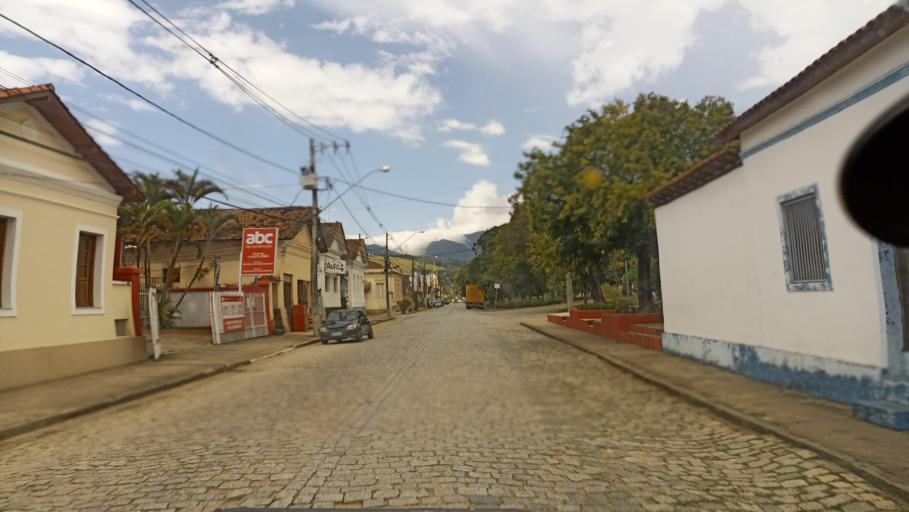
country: BR
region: Minas Gerais
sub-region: Passa Quatro
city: Passa Quatro
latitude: -22.3823
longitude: -44.9665
